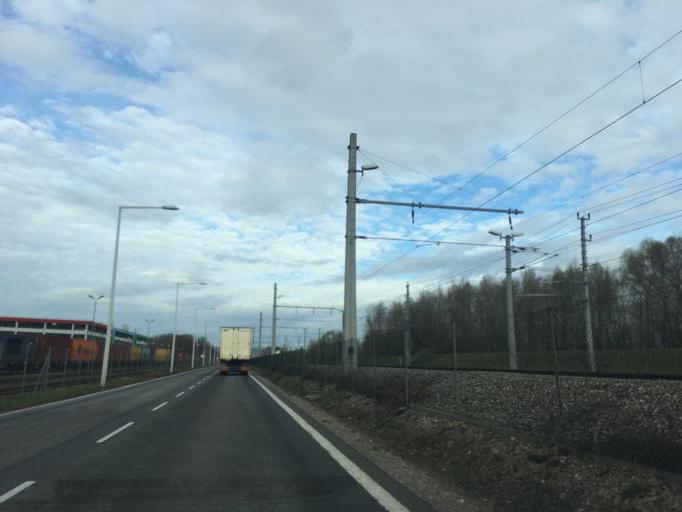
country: AT
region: Lower Austria
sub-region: Politischer Bezirk Wien-Umgebung
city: Schwechat
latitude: 48.1857
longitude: 16.4622
